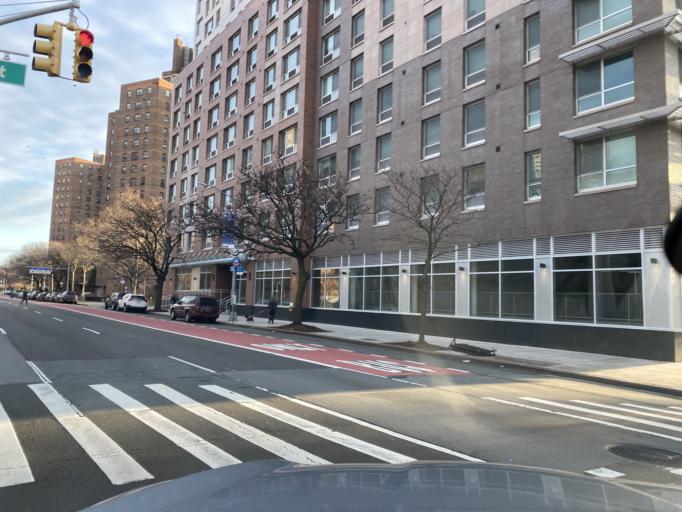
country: US
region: New York
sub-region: New York County
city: Manhattan
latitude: 40.7986
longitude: -73.9337
